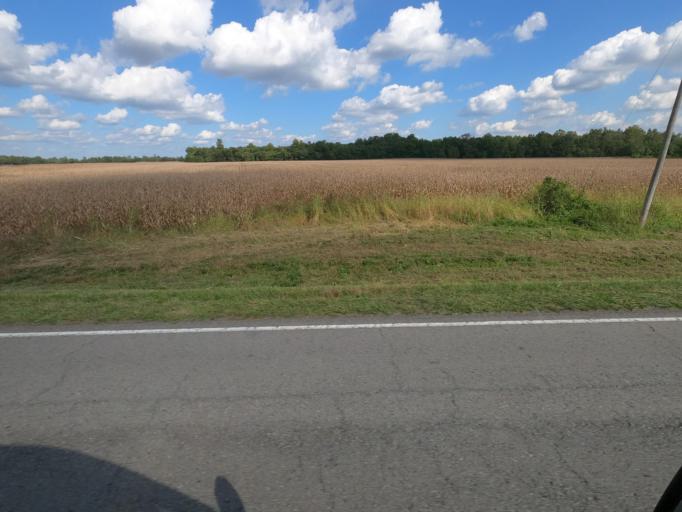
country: US
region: Illinois
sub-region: Massac County
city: Metropolis
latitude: 37.2809
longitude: -88.7575
